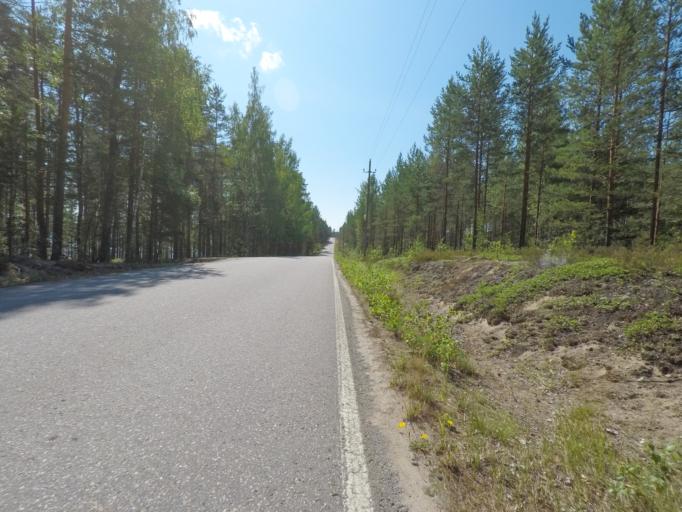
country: FI
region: Southern Savonia
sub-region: Mikkeli
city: Puumala
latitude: 61.4594
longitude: 28.1750
